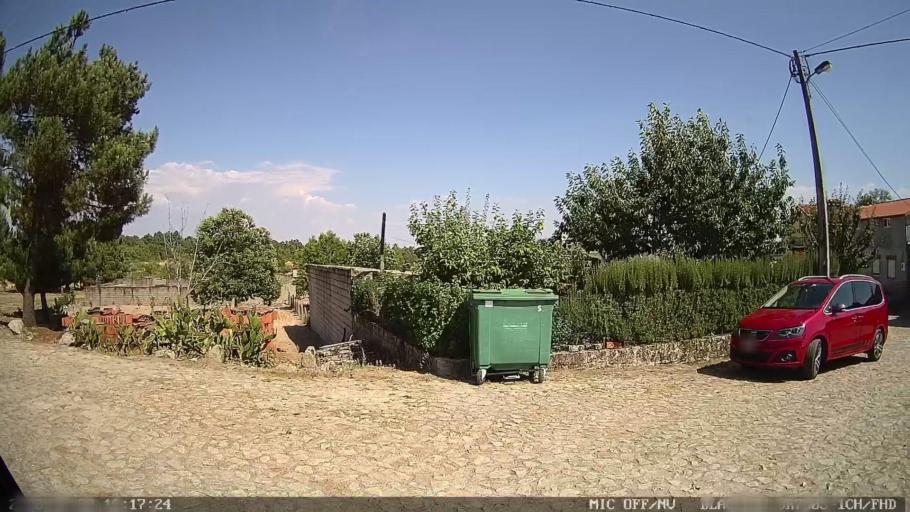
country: PT
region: Vila Real
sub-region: Murca
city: Murca
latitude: 41.3290
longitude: -7.4900
